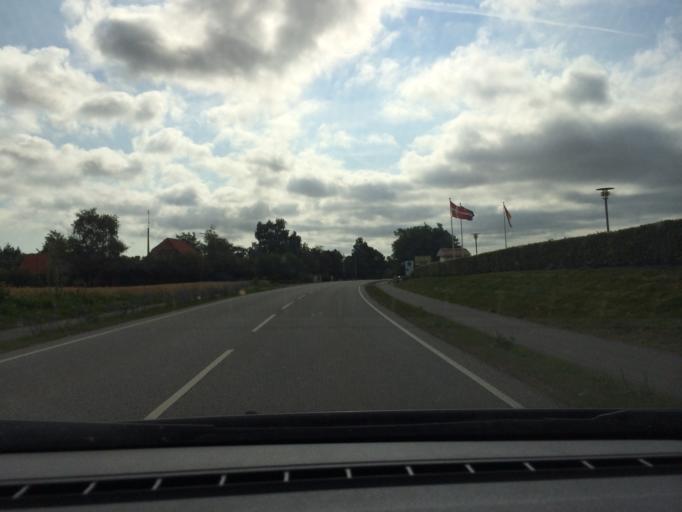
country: DK
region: Zealand
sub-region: Vordingborg Kommune
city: Stege
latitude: 54.9916
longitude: 12.3509
